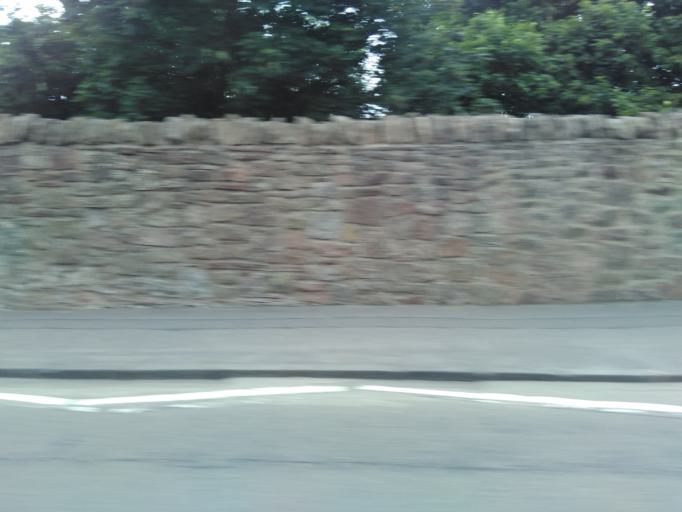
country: GB
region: Scotland
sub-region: Midlothian
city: Loanhead
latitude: 55.9155
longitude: -3.1503
